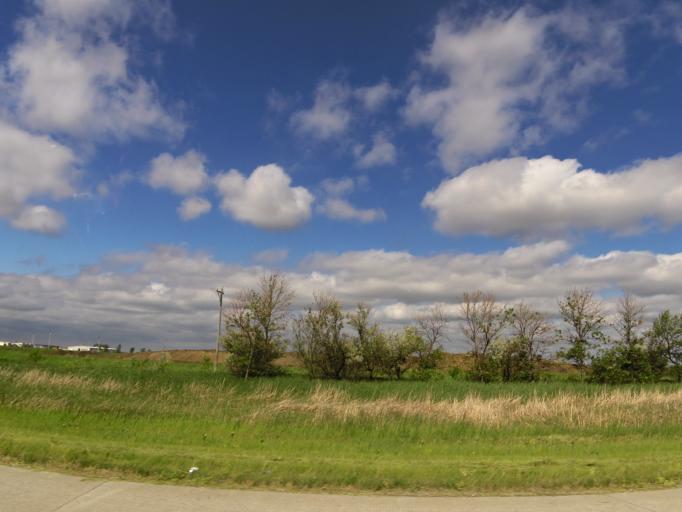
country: US
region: North Dakota
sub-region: Grand Forks County
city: Grand Forks
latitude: 47.9465
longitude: -97.0937
